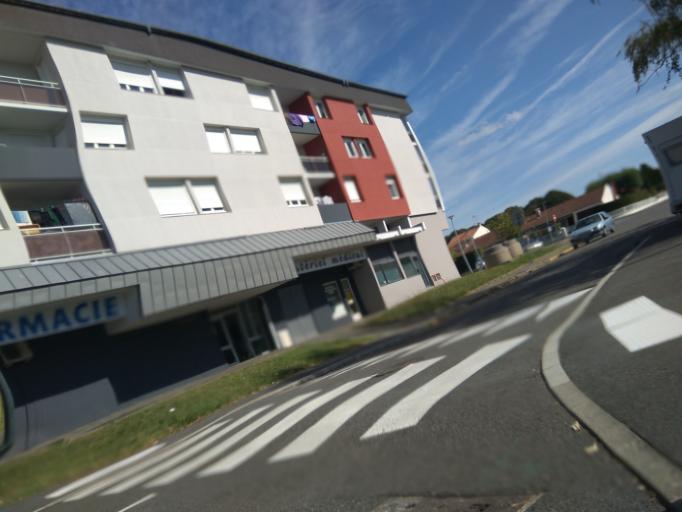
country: FR
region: Aquitaine
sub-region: Departement des Pyrenees-Atlantiques
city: Pau
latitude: 43.3138
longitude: -0.3451
